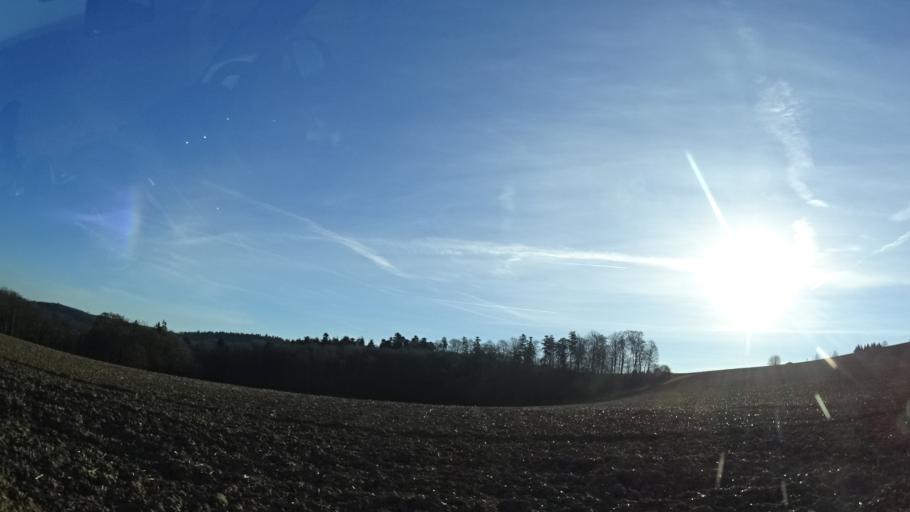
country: DE
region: Rheinland-Pfalz
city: Ruppertsecken
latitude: 49.6496
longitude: 7.8808
